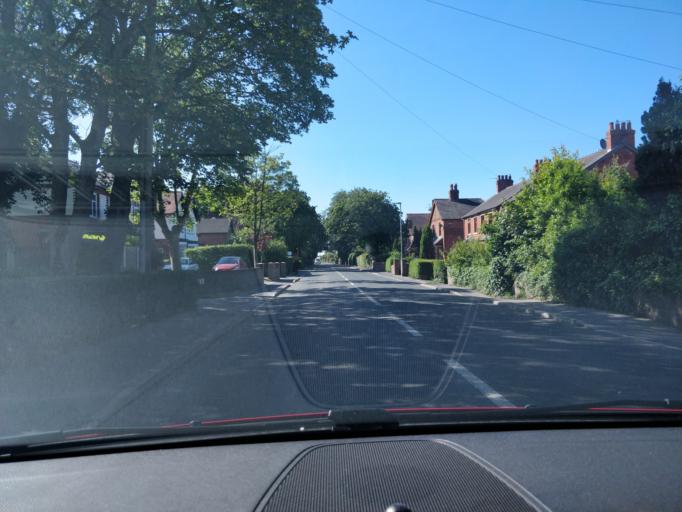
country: GB
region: England
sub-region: Lancashire
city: Tarleton
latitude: 53.6957
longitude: -2.8374
